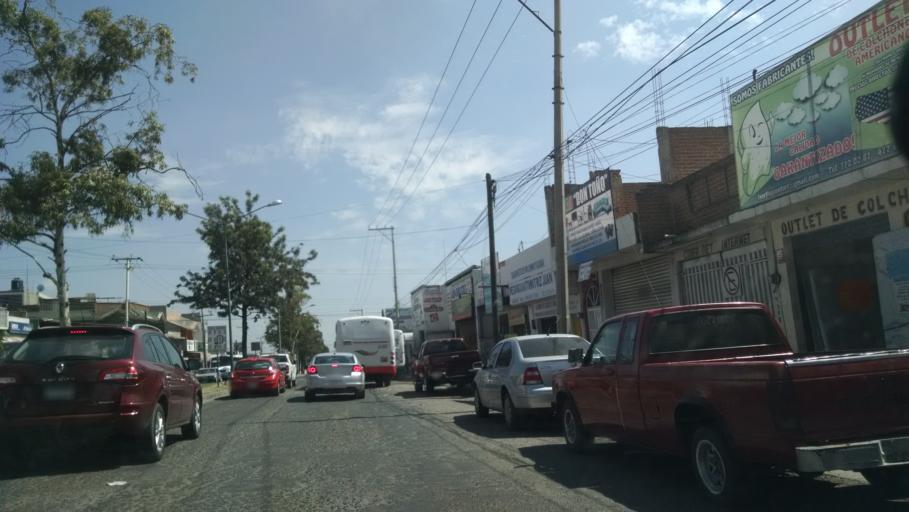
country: MX
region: Guanajuato
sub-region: Leon
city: Ejido la Joya
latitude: 21.1191
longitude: -101.7164
